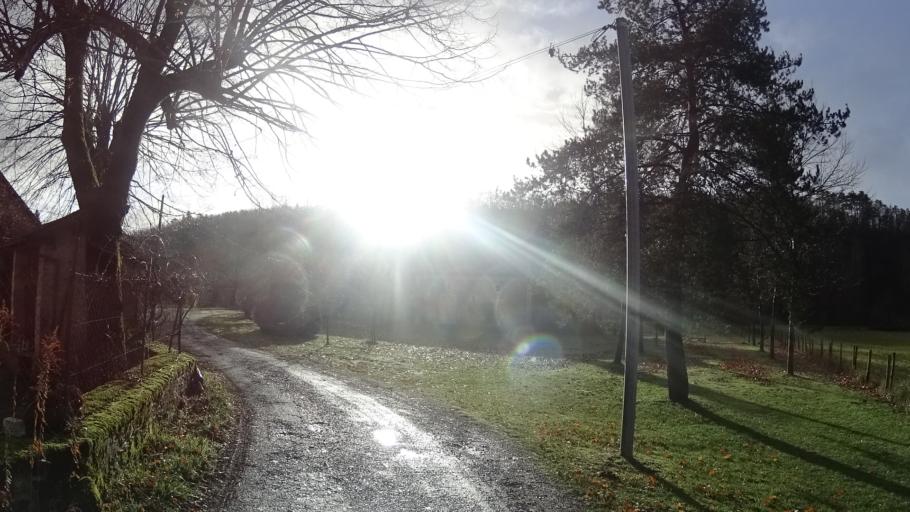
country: FR
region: Aquitaine
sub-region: Departement de la Dordogne
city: Sorges
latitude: 45.2725
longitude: 0.9338
